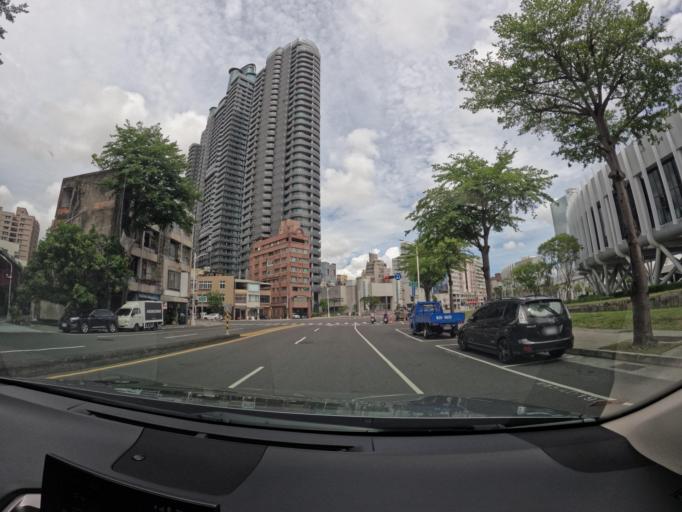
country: TW
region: Kaohsiung
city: Kaohsiung
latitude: 22.6194
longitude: 120.2925
